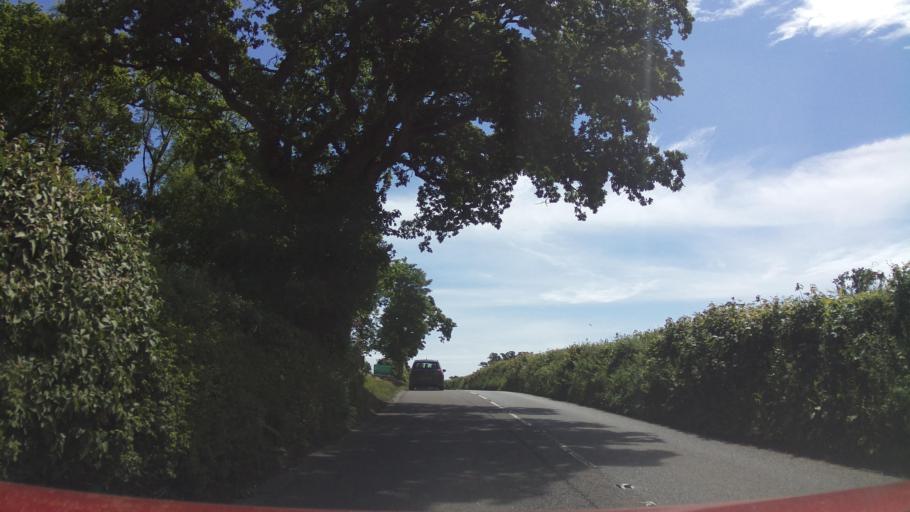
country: GB
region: England
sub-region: Devon
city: Uffculme
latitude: 50.8415
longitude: -3.3156
